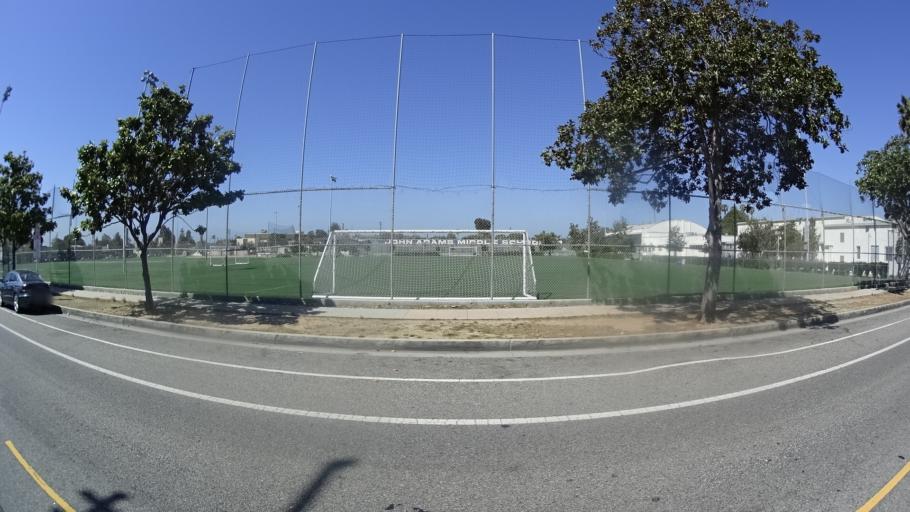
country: US
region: California
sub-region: Los Angeles County
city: Santa Monica
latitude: 34.0136
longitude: -118.4680
